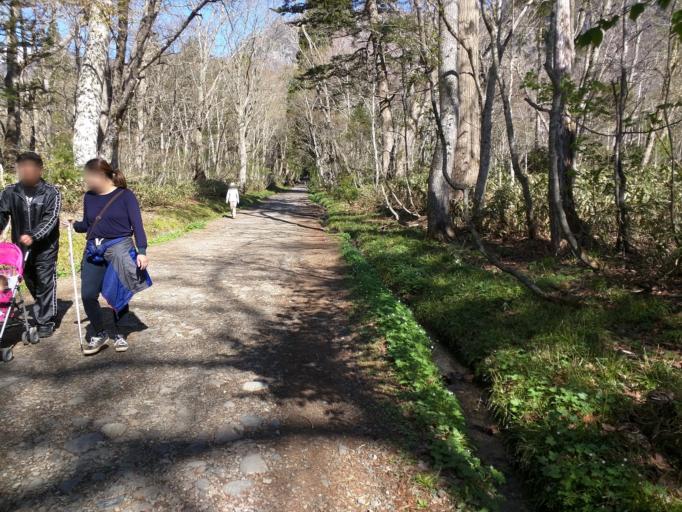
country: JP
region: Nagano
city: Nagano-shi
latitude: 36.7588
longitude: 138.0741
